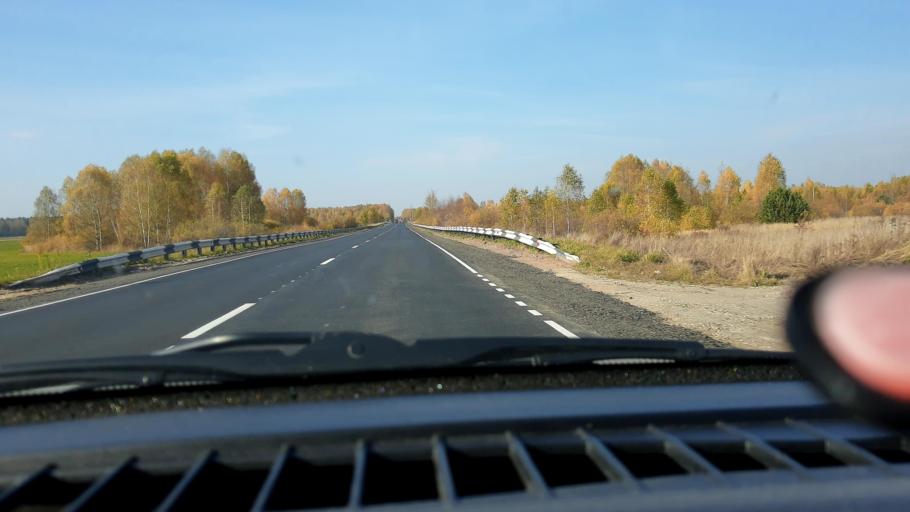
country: RU
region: Nizjnij Novgorod
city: Novaya Balakhna
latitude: 56.5839
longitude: 43.6791
